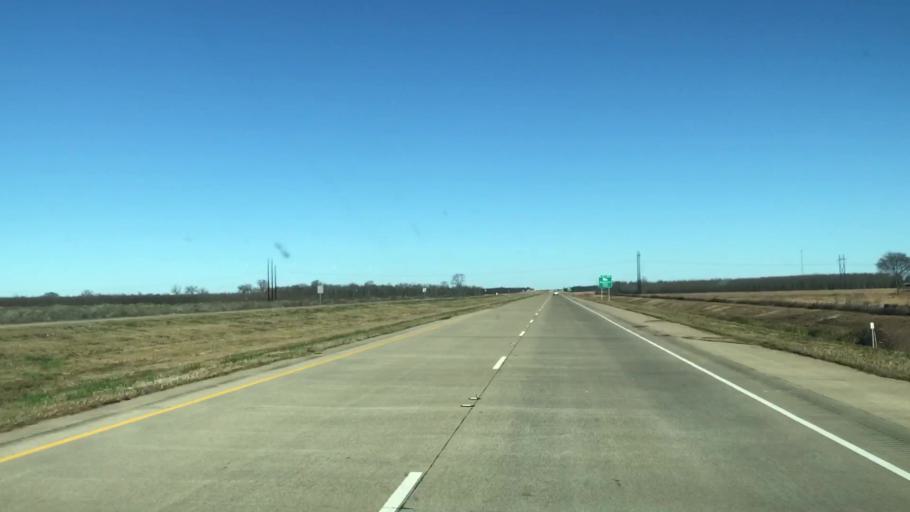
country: US
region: Louisiana
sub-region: Caddo Parish
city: Blanchard
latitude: 32.6617
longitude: -93.8446
